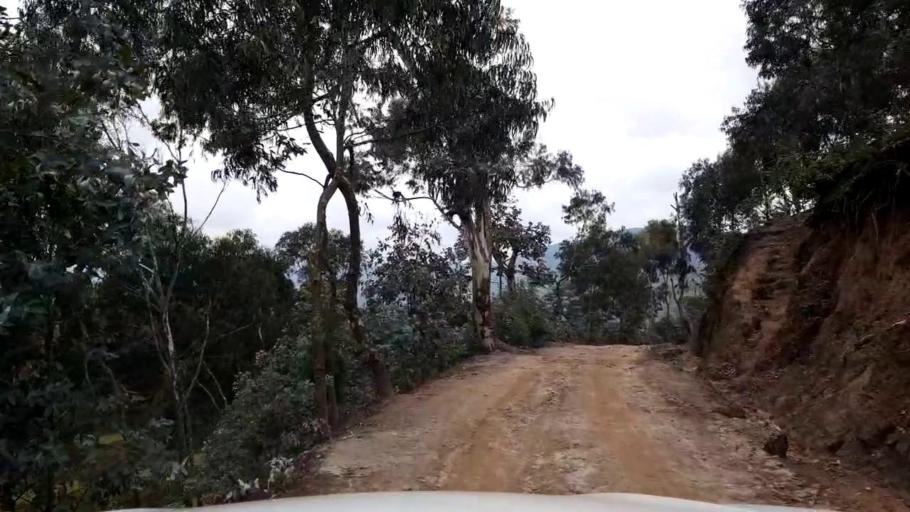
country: RW
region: Western Province
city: Kibuye
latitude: -1.9395
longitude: 29.4667
